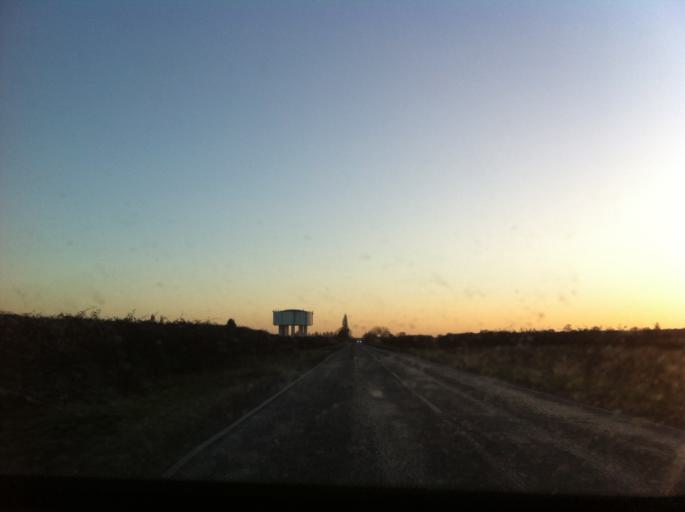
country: GB
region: England
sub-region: Northamptonshire
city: Irchester
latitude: 52.2628
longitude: -0.6562
